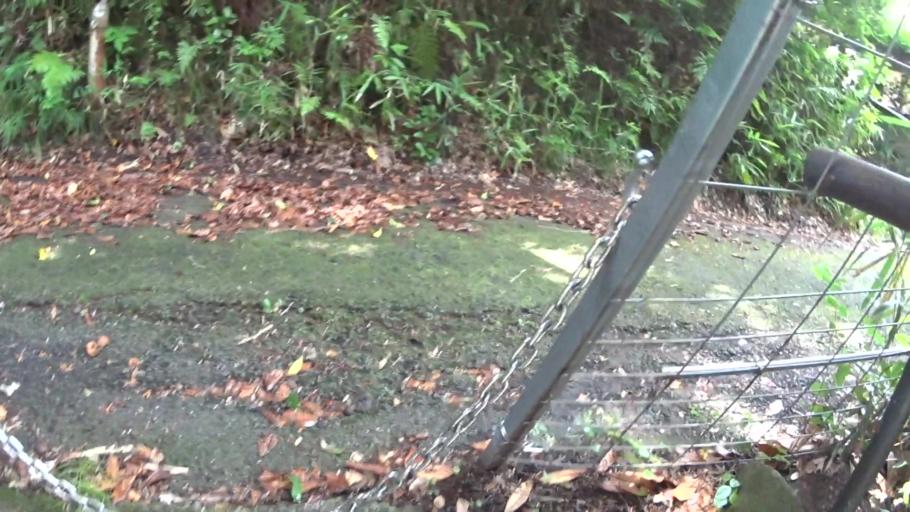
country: JP
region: Kyoto
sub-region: Kyoto-shi
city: Kamigyo-ku
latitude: 35.0255
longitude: 135.7976
